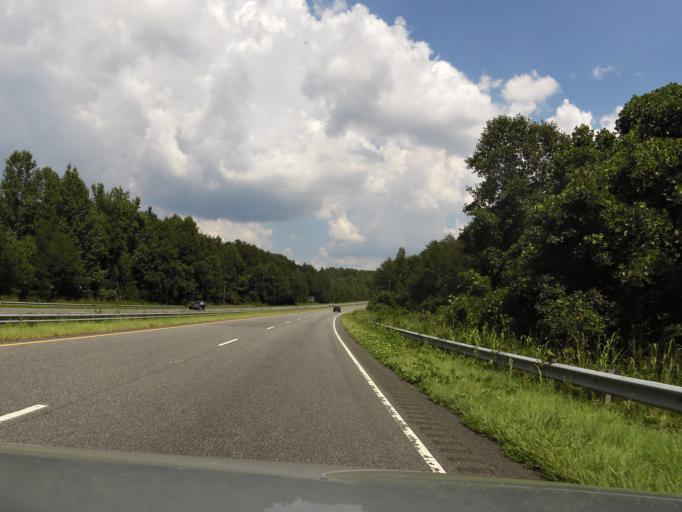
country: US
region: North Carolina
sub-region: Polk County
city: Columbus
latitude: 35.2662
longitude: -82.1707
